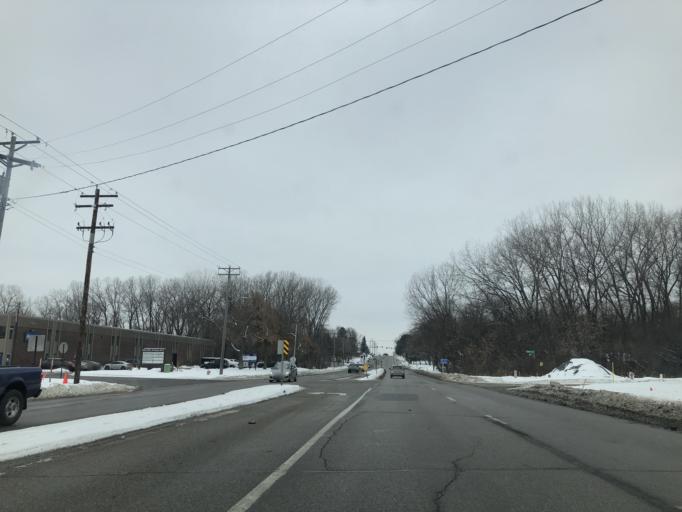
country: US
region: Minnesota
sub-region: Hennepin County
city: Osseo
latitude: 45.0946
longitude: -93.3861
